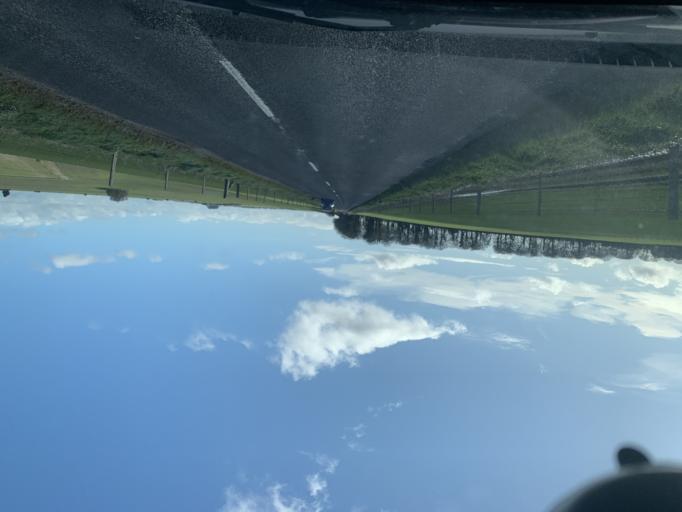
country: GB
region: England
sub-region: Wiltshire
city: Codford
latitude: 51.1878
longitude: -2.0459
